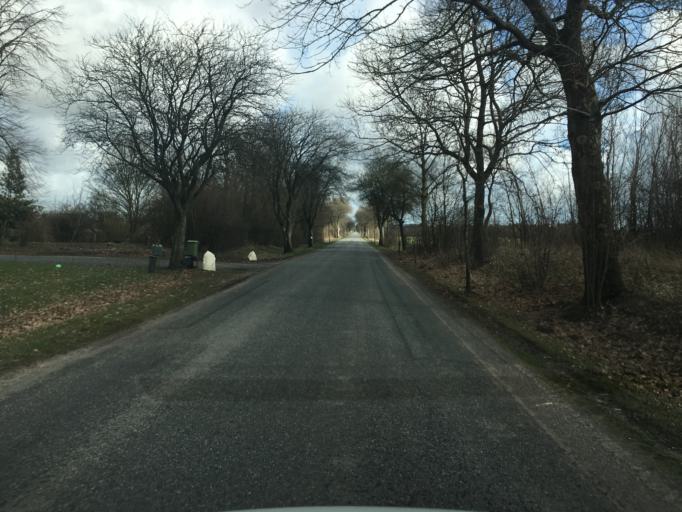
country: DK
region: South Denmark
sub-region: Aabenraa Kommune
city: Krusa
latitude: 54.9021
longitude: 9.3851
